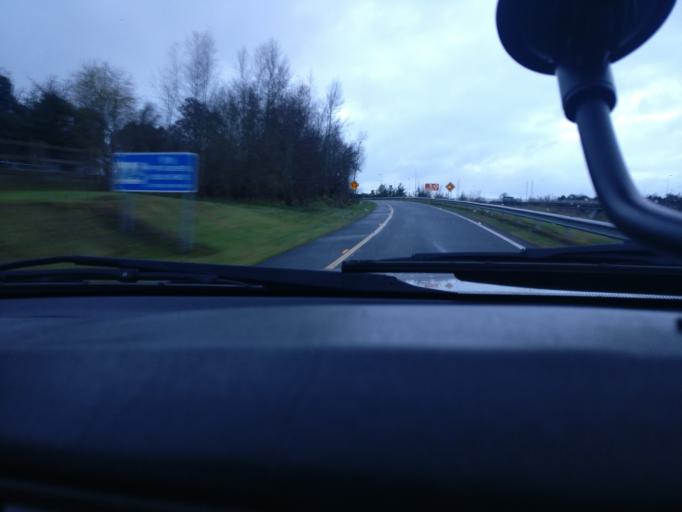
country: IE
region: Connaught
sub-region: County Galway
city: Ballinasloe
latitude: 53.3157
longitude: -8.2414
